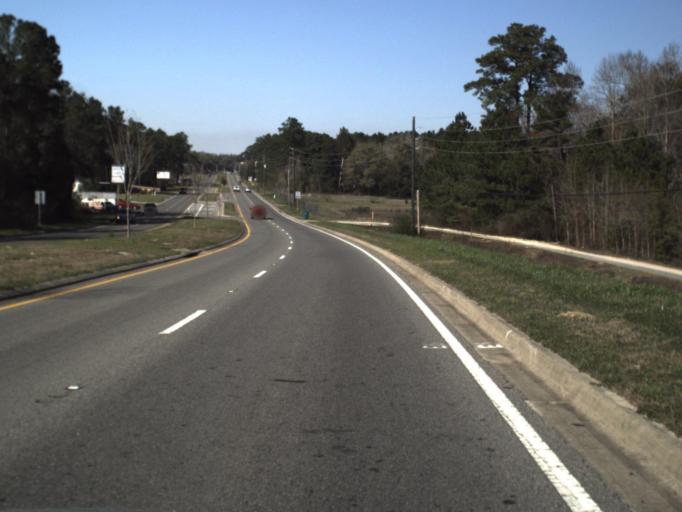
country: US
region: Florida
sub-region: Jackson County
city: Marianna
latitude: 30.7384
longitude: -85.1852
